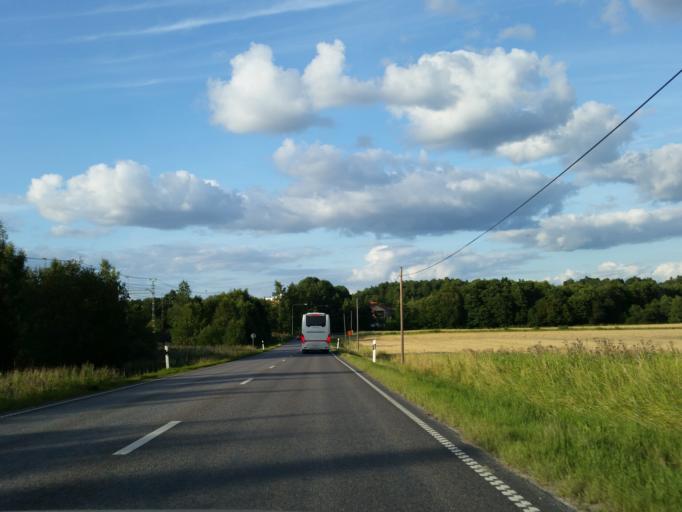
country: SE
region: Stockholm
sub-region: Sodertalje Kommun
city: Pershagen
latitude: 59.0809
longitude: 17.5488
